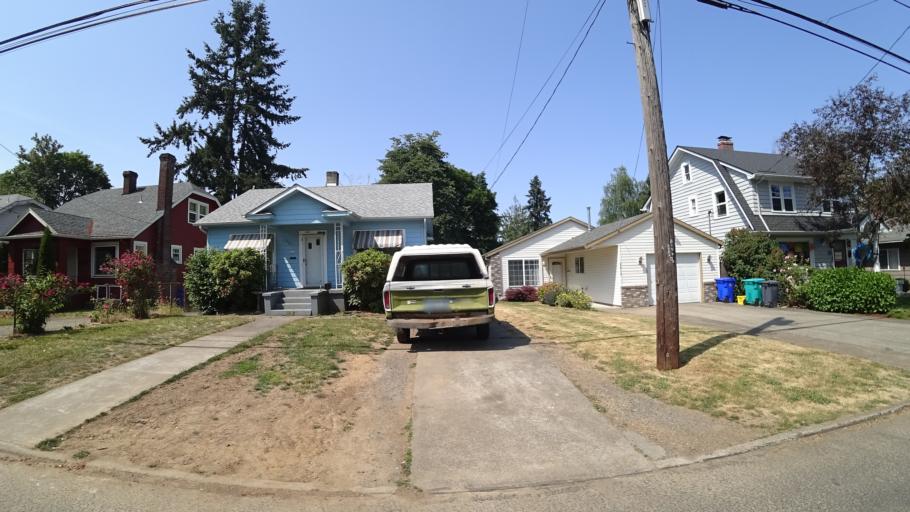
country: US
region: Oregon
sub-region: Multnomah County
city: Portland
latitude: 45.5791
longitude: -122.7010
